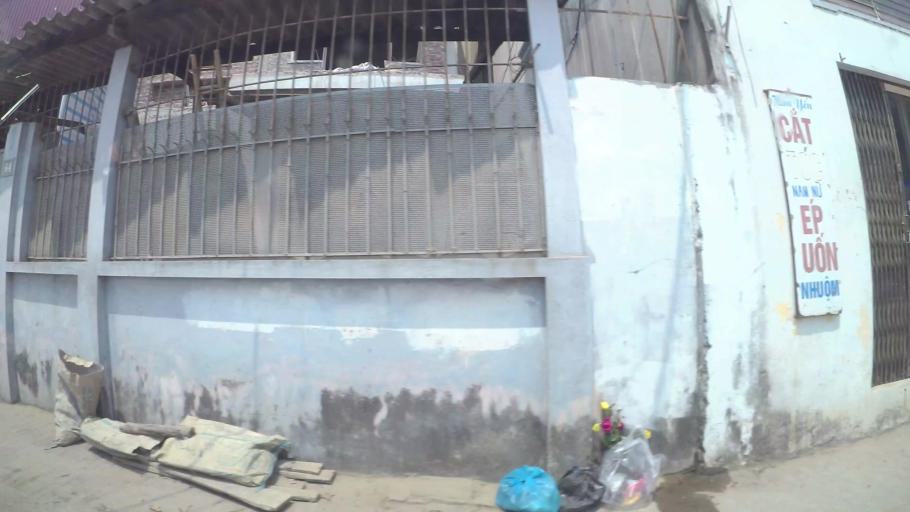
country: VN
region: Ha Noi
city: Van Dien
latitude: 20.9517
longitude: 105.8292
